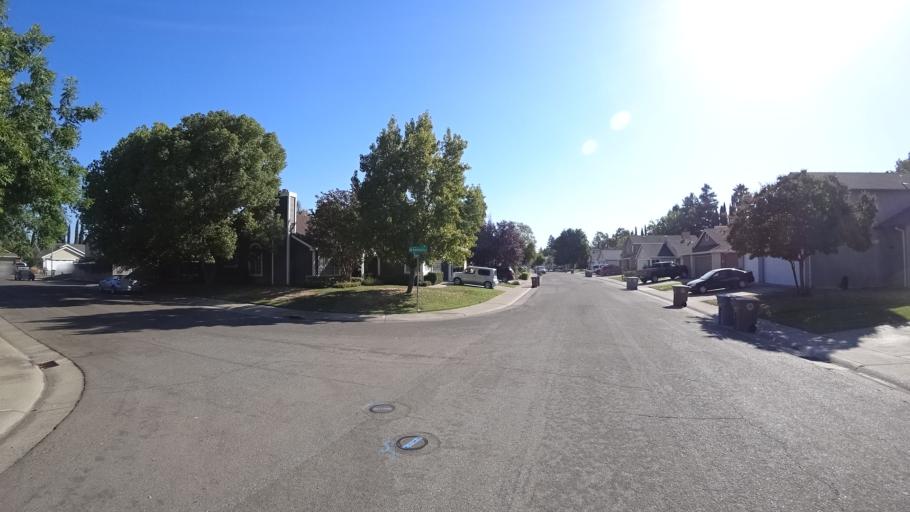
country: US
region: California
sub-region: Sacramento County
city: Laguna
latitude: 38.4347
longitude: -121.4449
